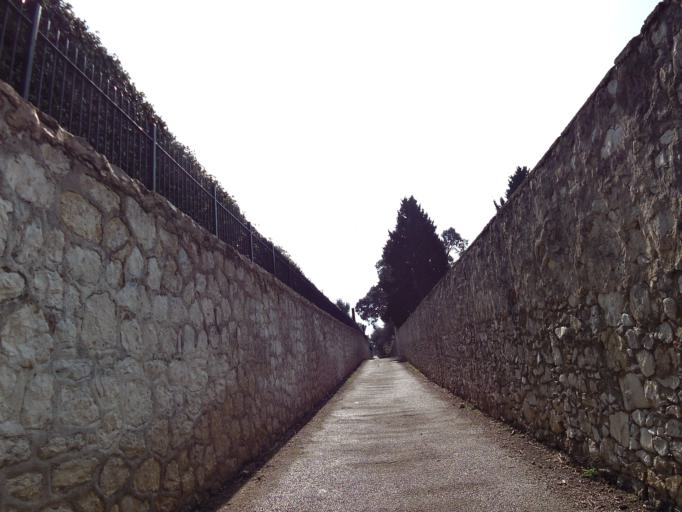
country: FR
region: Provence-Alpes-Cote d'Azur
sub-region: Departement des Alpes-Maritimes
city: Antibes
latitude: 43.5466
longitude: 7.1331
